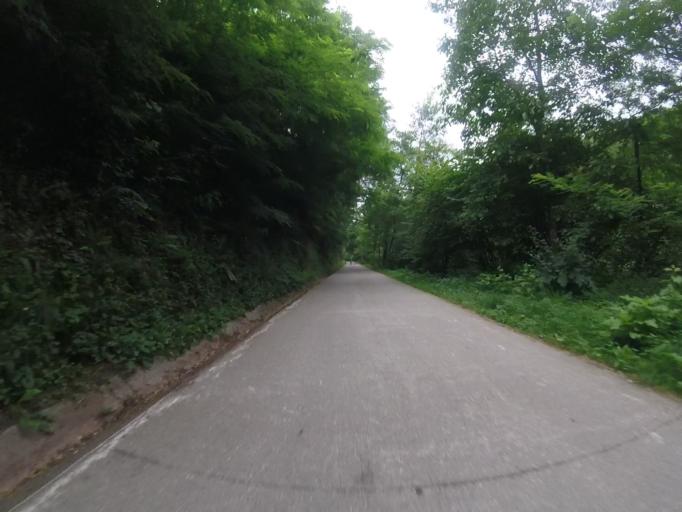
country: ES
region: Navarre
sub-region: Provincia de Navarra
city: Doneztebe
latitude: 43.1369
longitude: -1.6656
